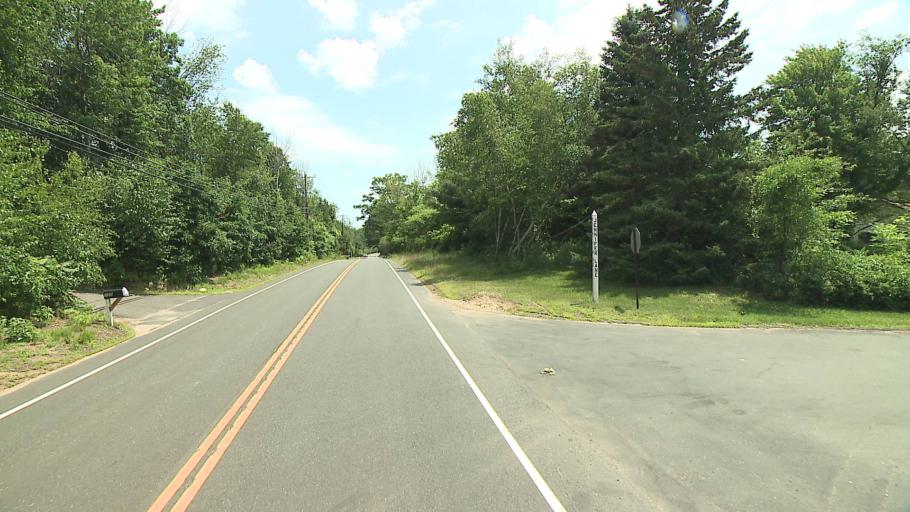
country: US
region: Connecticut
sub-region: Hartford County
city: North Granby
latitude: 41.9958
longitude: -72.8832
